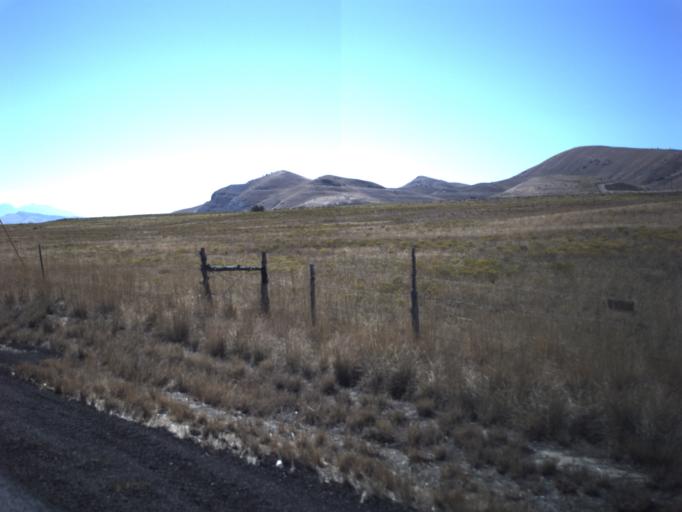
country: US
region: Utah
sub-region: Utah County
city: Saratoga Springs
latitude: 40.2815
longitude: -111.8720
